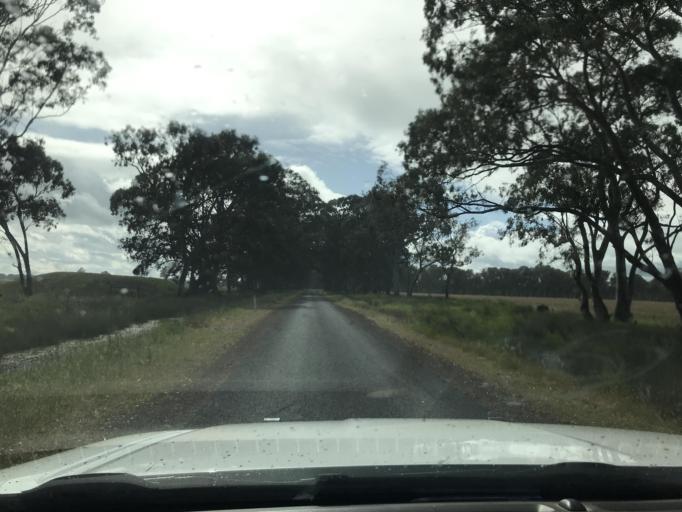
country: AU
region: South Australia
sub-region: Wattle Range
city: Penola
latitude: -37.1899
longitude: 141.2520
